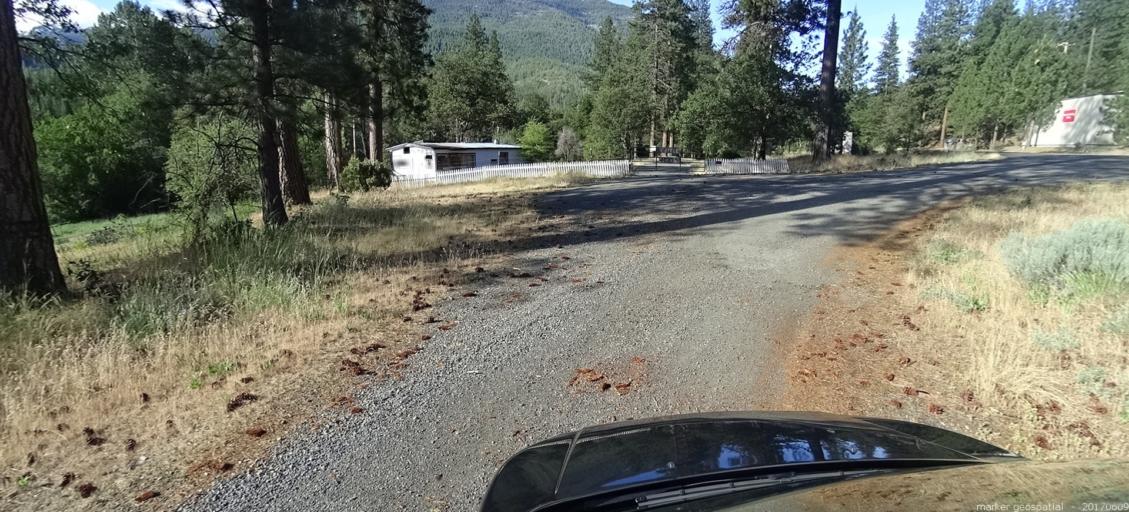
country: US
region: California
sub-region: Siskiyou County
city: Weed
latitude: 41.3083
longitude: -122.7726
